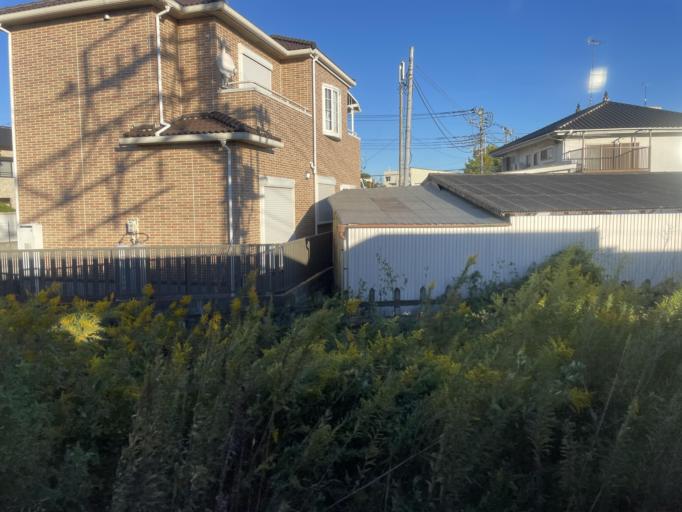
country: JP
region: Saitama
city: Satte
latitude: 36.0759
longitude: 139.7152
